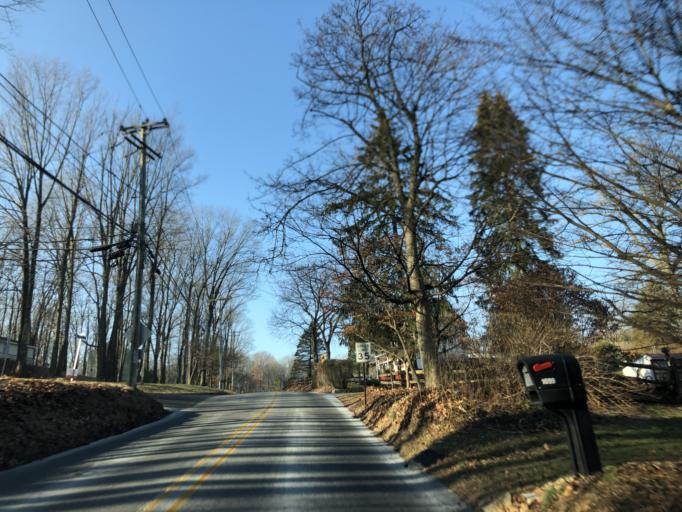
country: US
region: Pennsylvania
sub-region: Chester County
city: Downingtown
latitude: 39.9897
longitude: -75.7131
